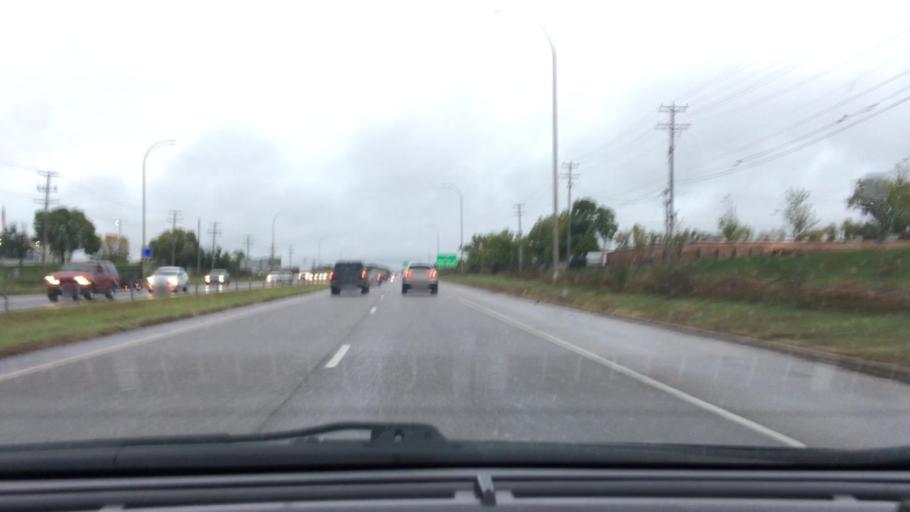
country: US
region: Minnesota
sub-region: Hennepin County
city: New Hope
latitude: 45.0498
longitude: -93.4008
